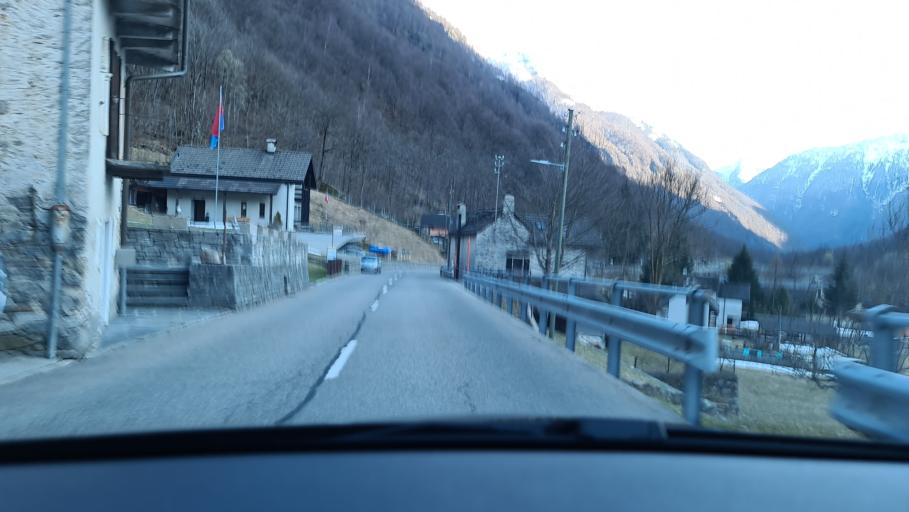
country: CH
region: Ticino
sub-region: Locarno District
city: Lavertezzo
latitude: 46.3364
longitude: 8.8052
